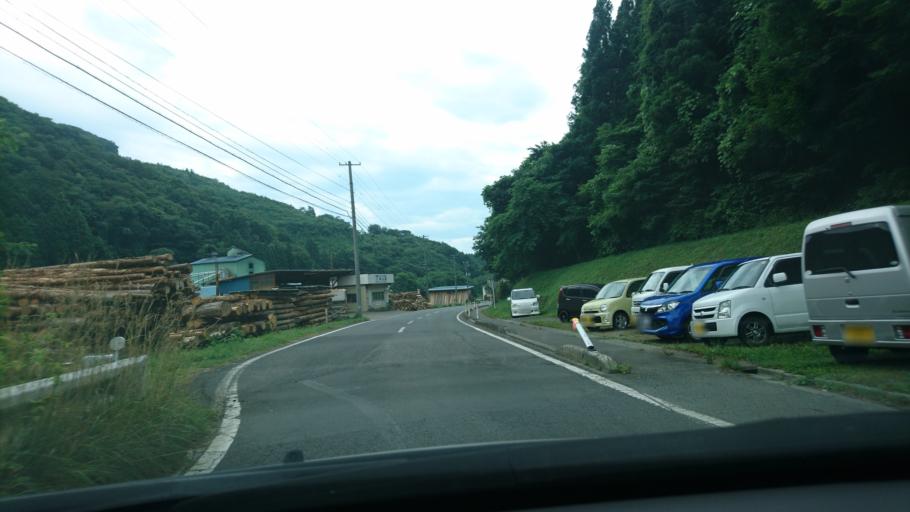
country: JP
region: Iwate
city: Ichinoseki
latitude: 38.8419
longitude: 141.4293
